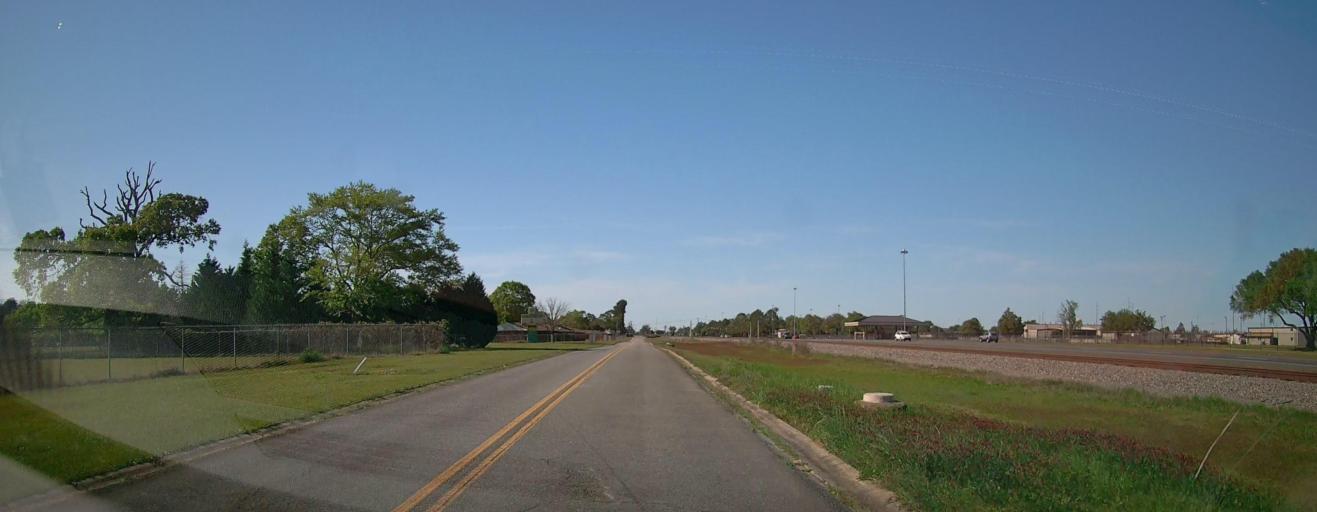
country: US
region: Georgia
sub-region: Houston County
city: Robins Air Force Base
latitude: 32.6087
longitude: -83.5965
